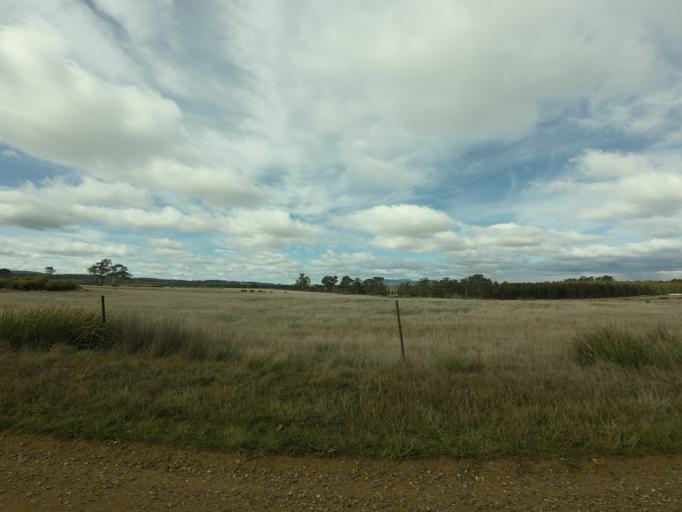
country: AU
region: Tasmania
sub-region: Brighton
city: Bridgewater
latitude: -42.4365
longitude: 147.3859
